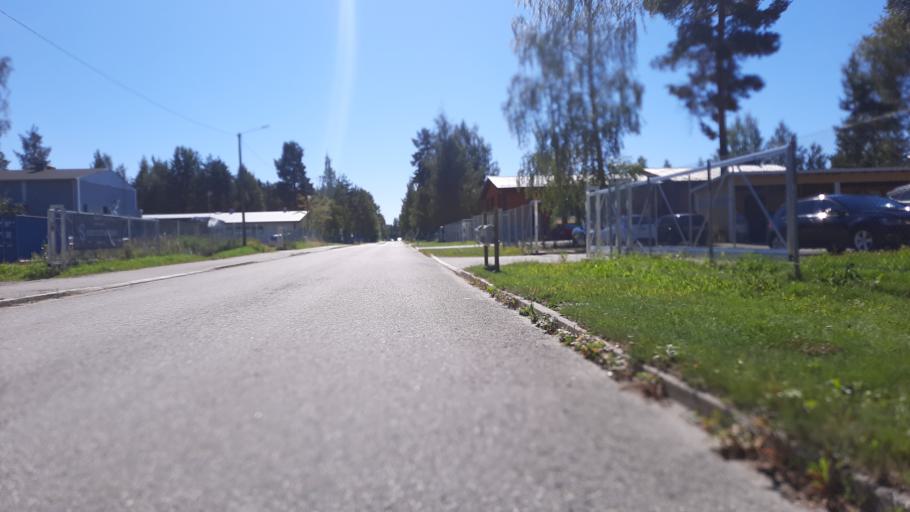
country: FI
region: North Karelia
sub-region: Joensuu
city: Joensuu
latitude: 62.6236
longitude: 29.7435
